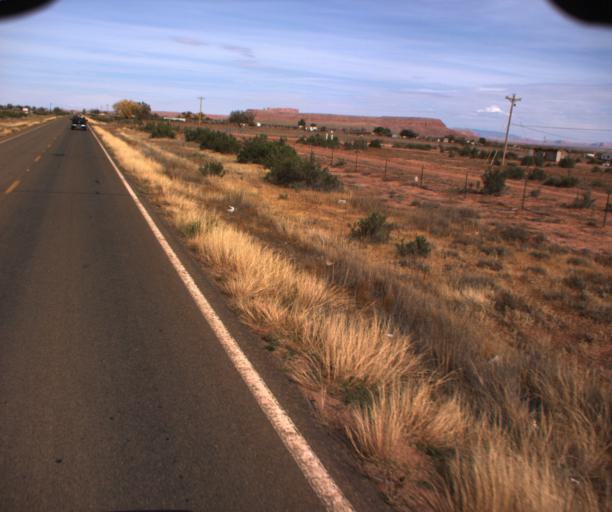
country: US
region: Arizona
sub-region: Apache County
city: Many Farms
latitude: 36.4038
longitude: -109.6085
